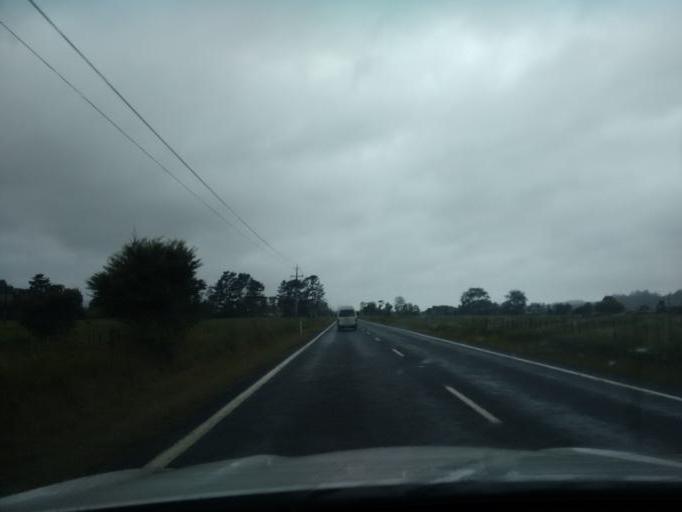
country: NZ
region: Waikato
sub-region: Thames-Coromandel District
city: Whitianga
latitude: -36.8554
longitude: 175.6529
